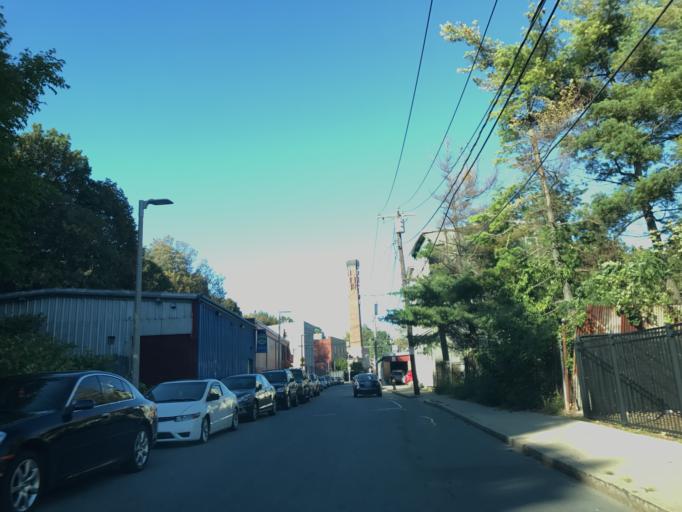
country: US
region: Massachusetts
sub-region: Norfolk County
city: Brookline
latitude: 42.3275
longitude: -71.0985
